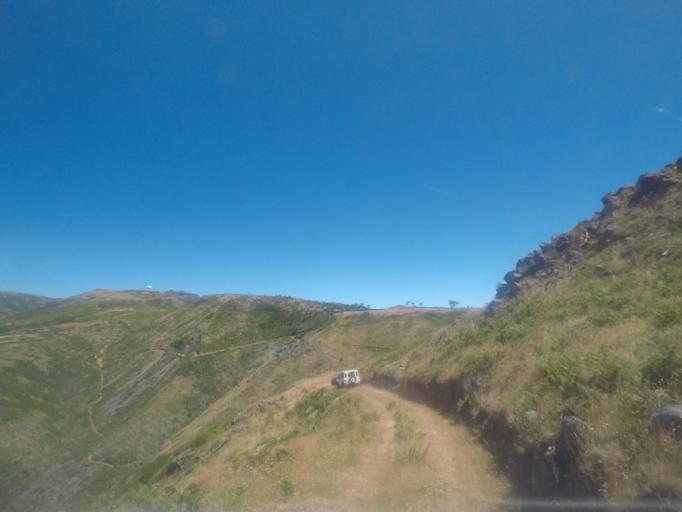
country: PT
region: Madeira
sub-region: Funchal
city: Nossa Senhora do Monte
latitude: 32.7114
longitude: -16.9139
